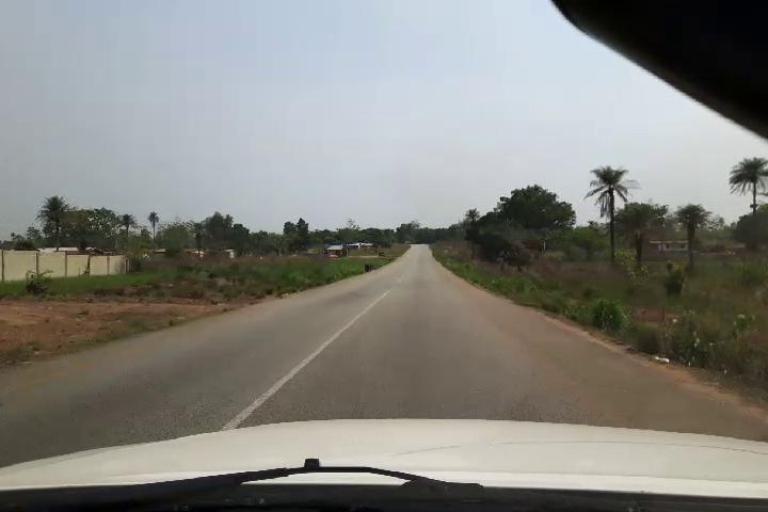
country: SL
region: Southern Province
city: Largo
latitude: 8.3138
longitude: -12.2175
